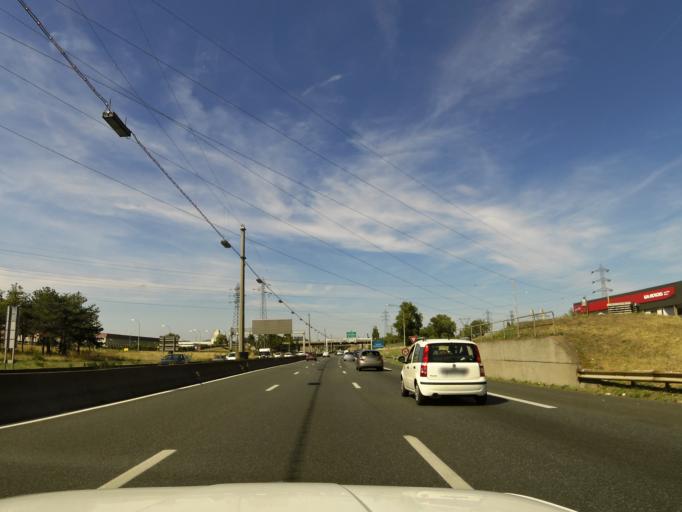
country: FR
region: Rhone-Alpes
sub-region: Departement du Rhone
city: Saint-Fons
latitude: 45.7118
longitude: 4.8434
